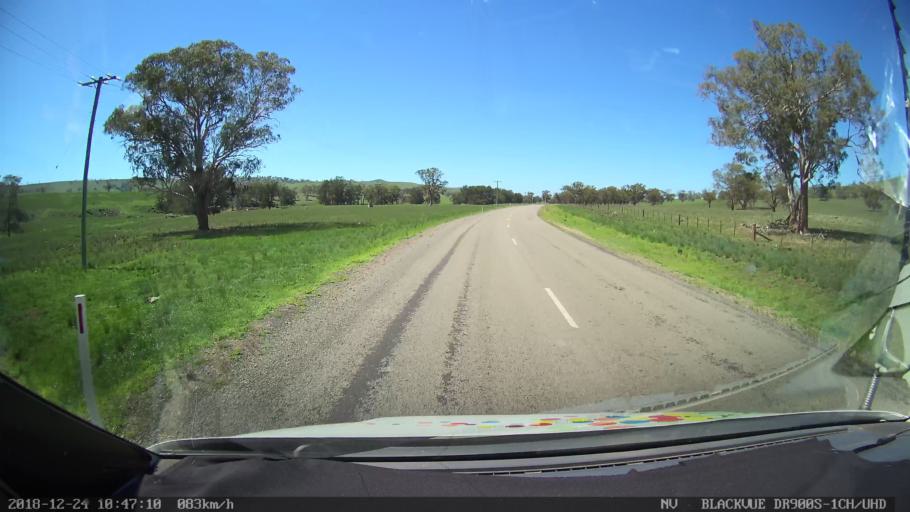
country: AU
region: New South Wales
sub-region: Upper Hunter Shire
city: Merriwa
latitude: -31.9210
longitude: 150.4294
